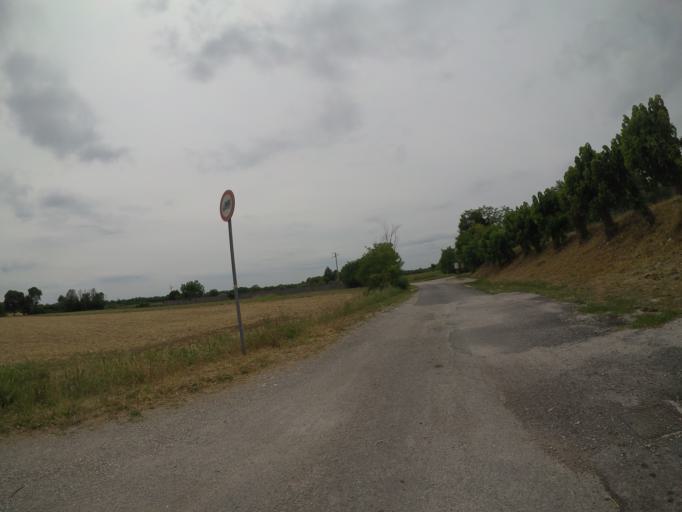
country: IT
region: Friuli Venezia Giulia
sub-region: Provincia di Udine
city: Pasian di Prato
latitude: 46.0493
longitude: 13.1819
